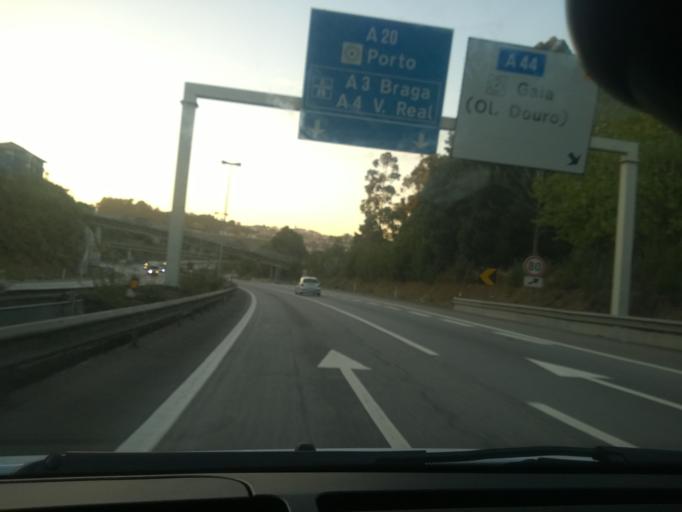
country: PT
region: Porto
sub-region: Vila Nova de Gaia
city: Oliveira do Douro
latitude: 41.1349
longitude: -8.5774
